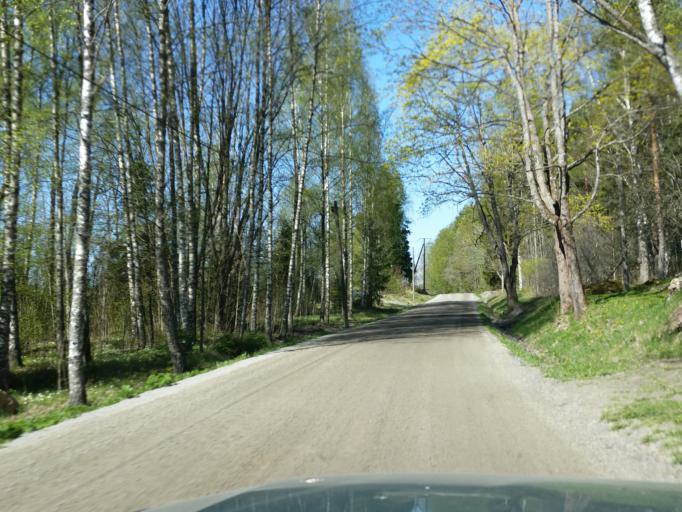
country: FI
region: Uusimaa
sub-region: Helsinki
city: Karjalohja
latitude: 60.1438
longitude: 23.8187
